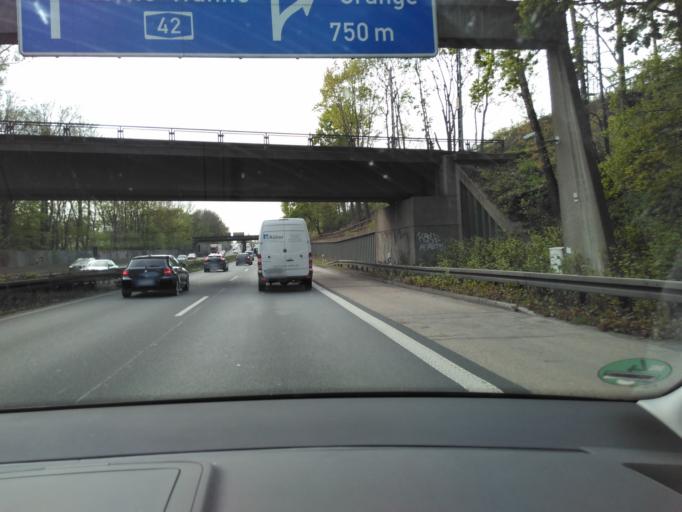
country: DE
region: North Rhine-Westphalia
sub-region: Regierungsbezirk Arnsberg
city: Herne
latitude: 51.5439
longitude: 7.1898
